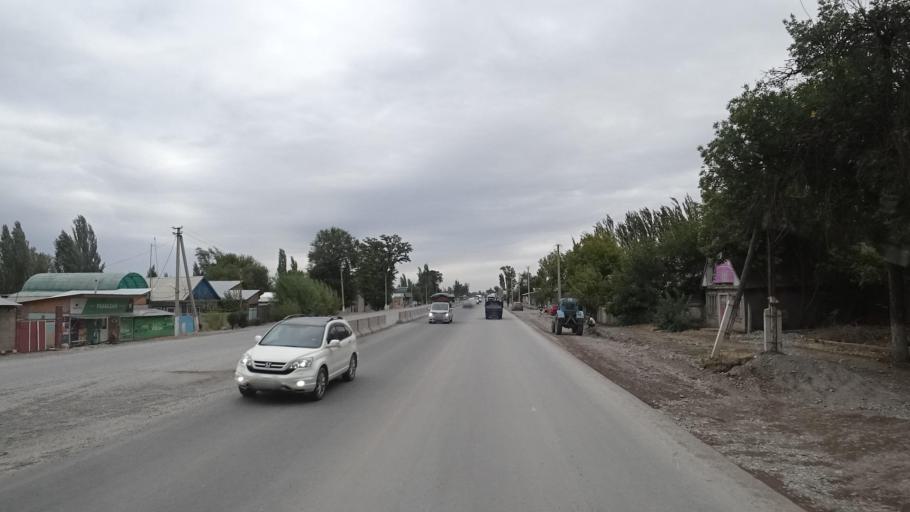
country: KG
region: Chuy
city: Belovodskoye
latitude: 42.8476
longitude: 74.1636
